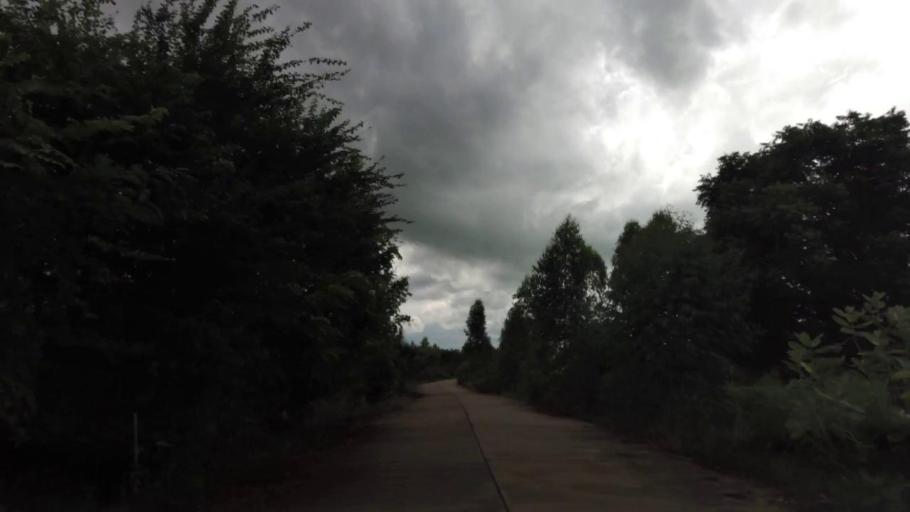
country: TH
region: Nakhon Sawan
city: Phai Sali
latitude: 15.6018
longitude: 100.6776
